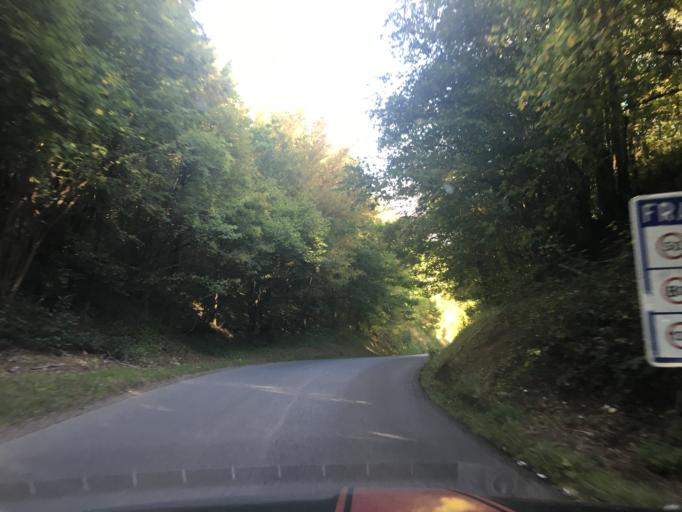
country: FR
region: Lorraine
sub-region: Departement de Meurthe-et-Moselle
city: Hussigny-Godbrange
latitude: 49.4992
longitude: 5.8698
